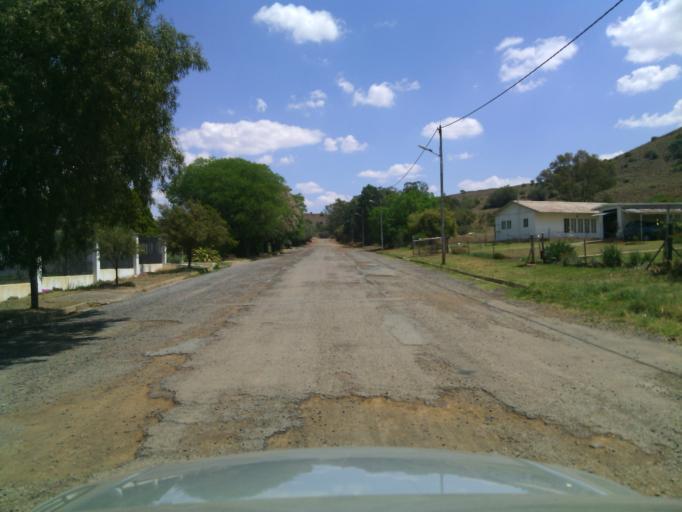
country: ZA
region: Orange Free State
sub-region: Xhariep District Municipality
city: Dewetsdorp
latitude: -29.5803
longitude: 26.6626
